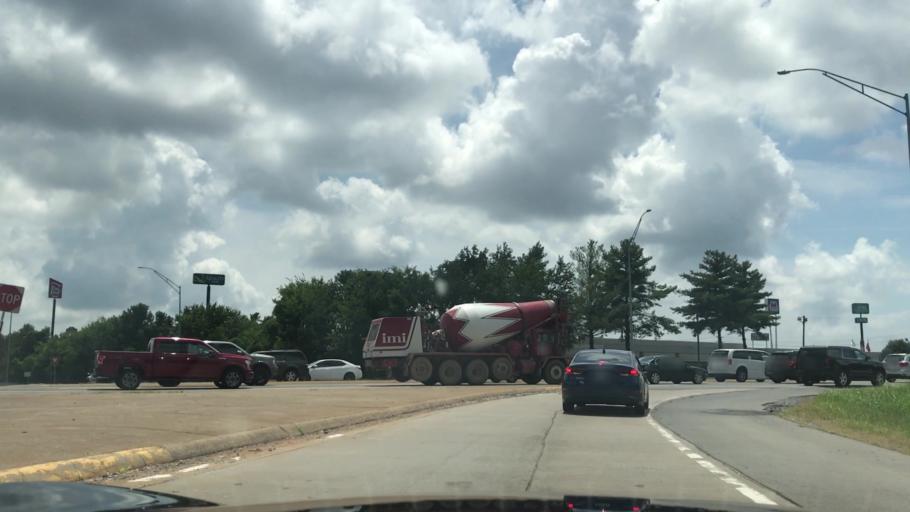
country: US
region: Tennessee
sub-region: Montgomery County
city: Clarksville
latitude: 36.5989
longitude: -87.2844
